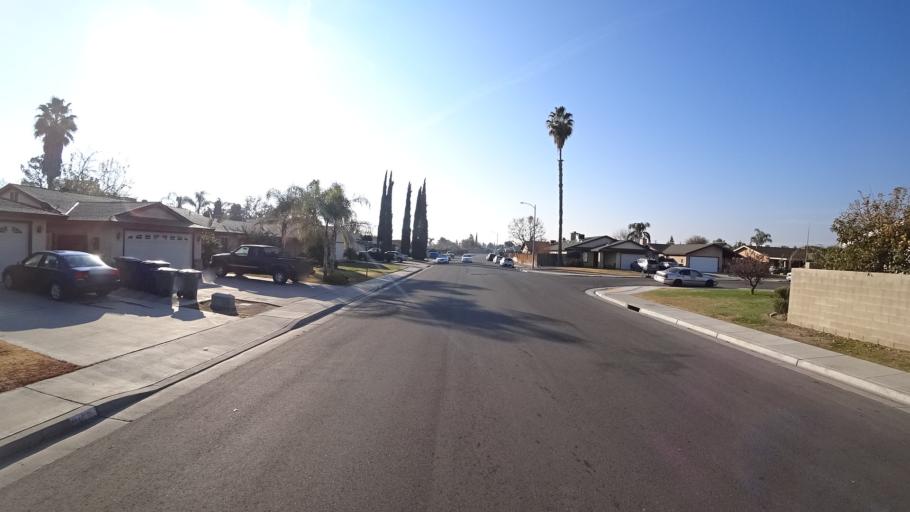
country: US
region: California
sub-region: Kern County
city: Greenfield
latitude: 35.3050
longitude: -119.0240
